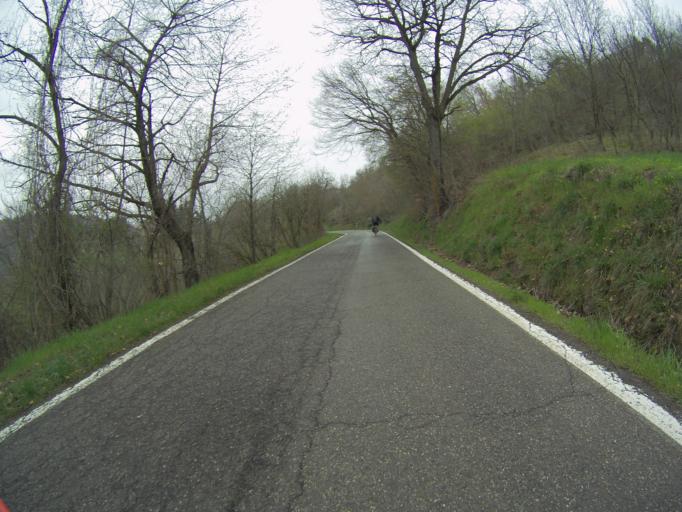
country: IT
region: Emilia-Romagna
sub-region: Provincia di Reggio Emilia
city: Casina
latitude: 44.5439
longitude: 10.4647
